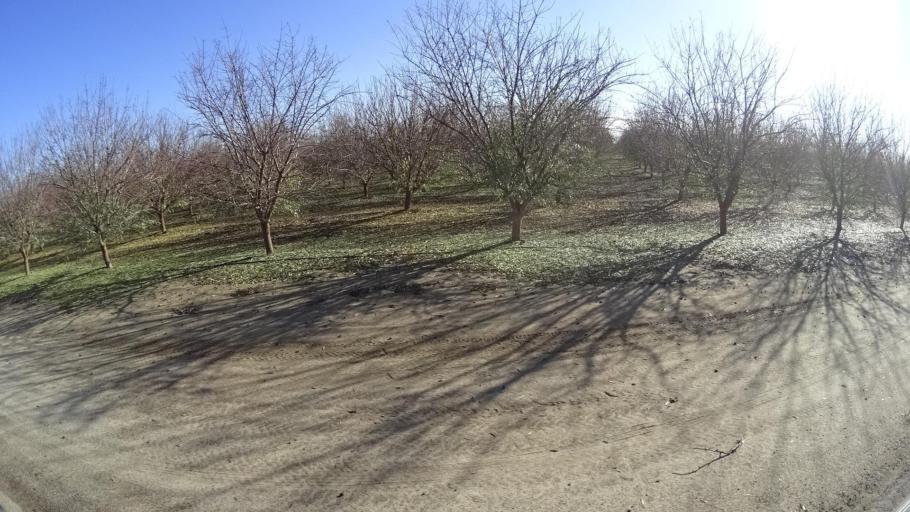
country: US
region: California
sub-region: Kern County
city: Delano
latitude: 35.7400
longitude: -119.3119
